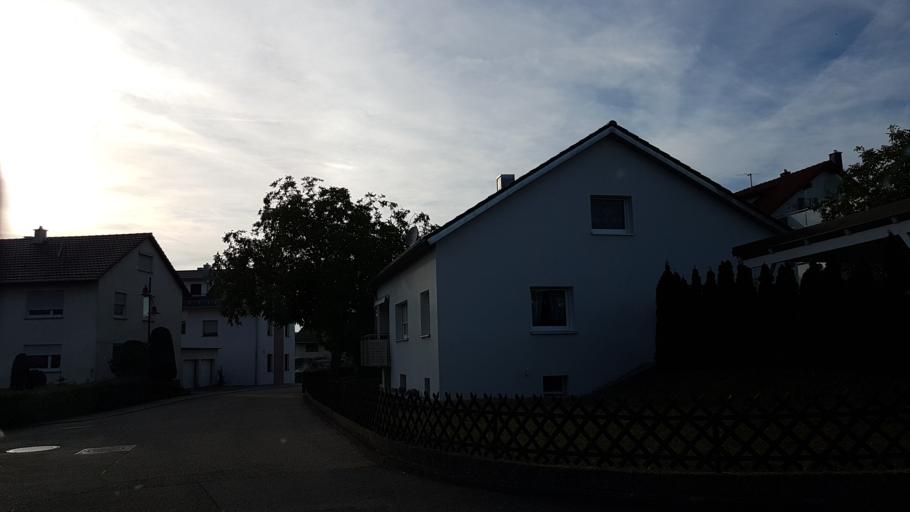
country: DE
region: Baden-Wuerttemberg
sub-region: Regierungsbezirk Stuttgart
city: Neuenstadt am Kocher
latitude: 49.2144
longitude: 9.3592
